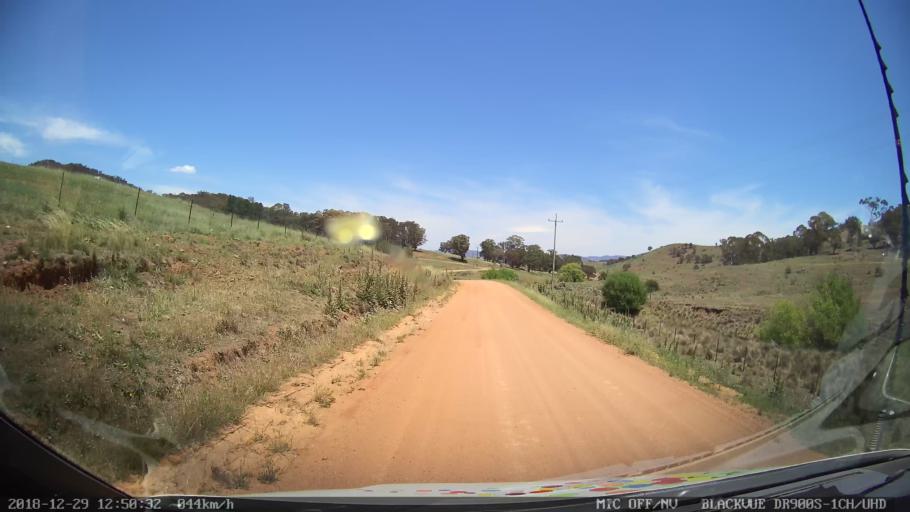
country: AU
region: Australian Capital Territory
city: Macarthur
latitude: -35.6704
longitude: 149.2029
